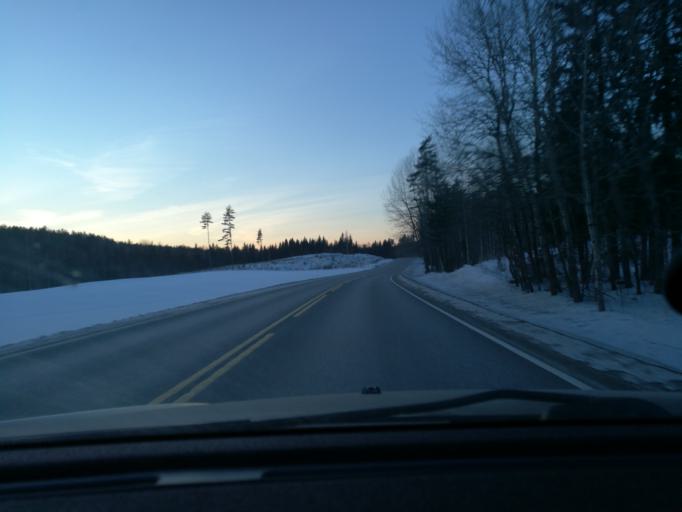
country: FI
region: Uusimaa
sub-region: Helsinki
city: Vihti
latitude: 60.3891
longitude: 24.5038
